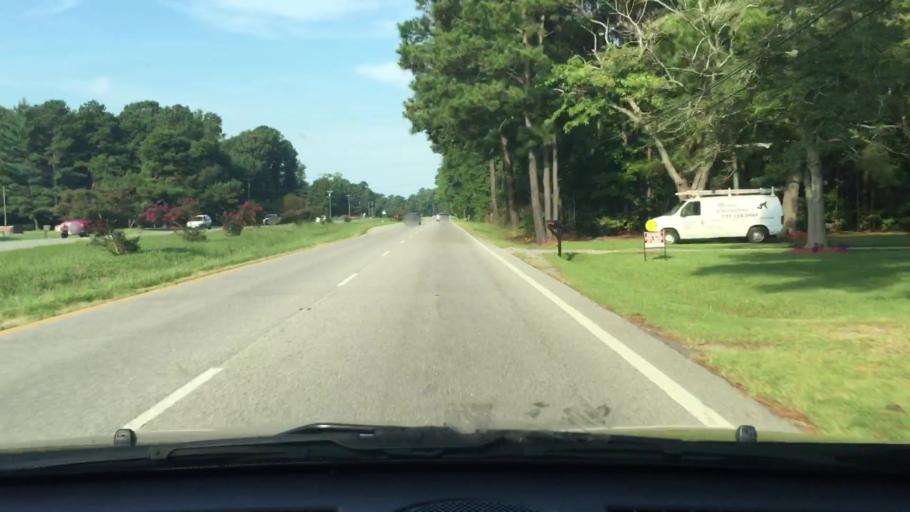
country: US
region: Virginia
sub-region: Isle of Wight County
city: Carrollton
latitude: 36.9414
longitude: -76.5662
